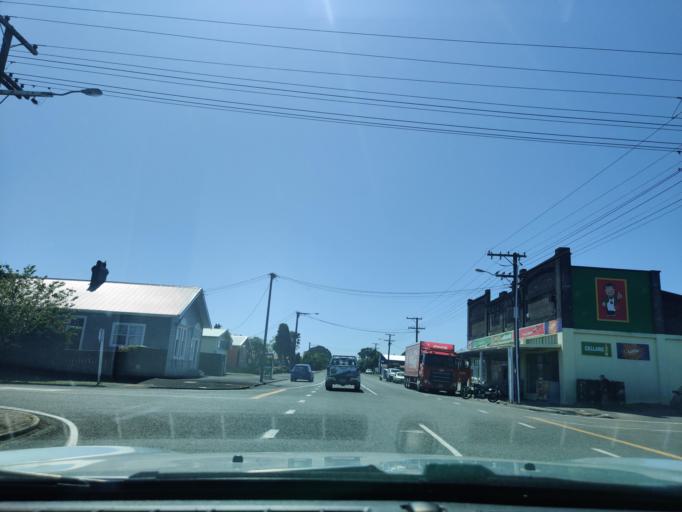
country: NZ
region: Taranaki
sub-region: South Taranaki District
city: Opunake
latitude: -39.3276
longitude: 173.8037
